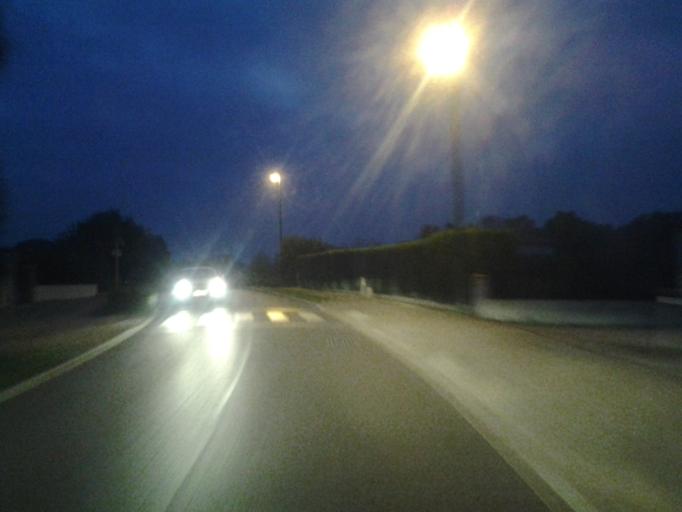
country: FR
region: Pays de la Loire
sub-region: Departement de la Vendee
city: Landeronde
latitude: 46.6547
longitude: -1.5642
